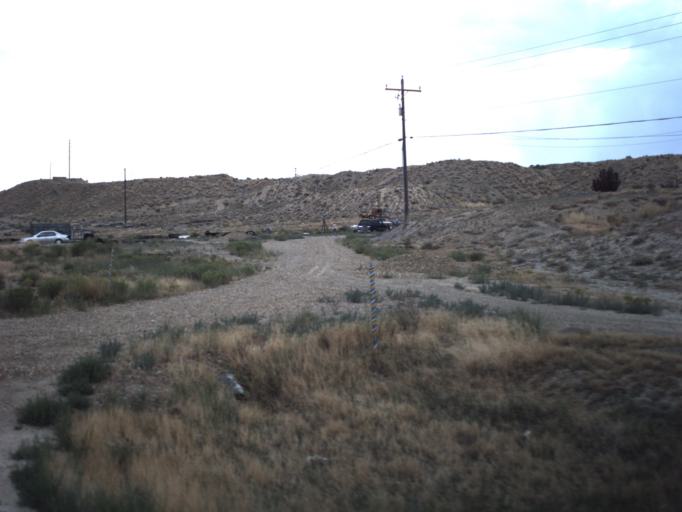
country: US
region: Utah
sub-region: Emery County
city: Huntington
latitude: 39.3722
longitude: -110.8520
